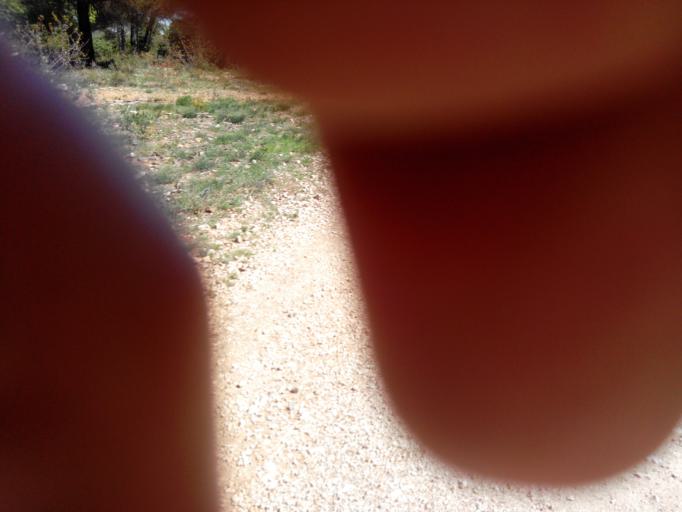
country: FR
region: Provence-Alpes-Cote d'Azur
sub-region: Departement des Bouches-du-Rhone
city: Auriol
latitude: 43.3553
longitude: 5.6729
